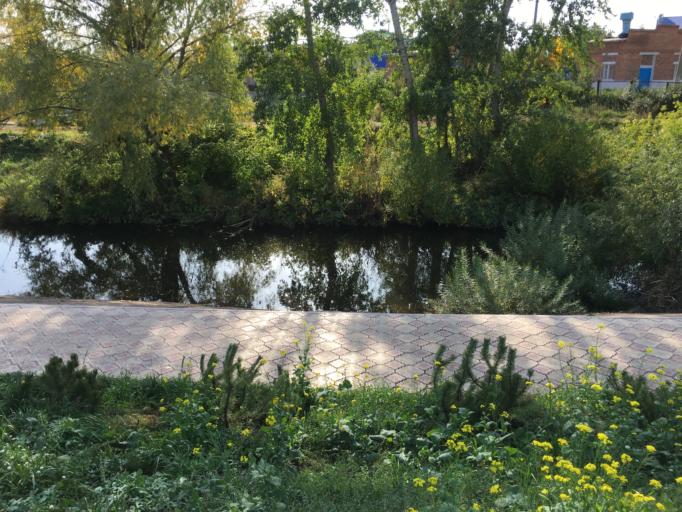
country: RU
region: Bashkortostan
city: Meleuz
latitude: 52.9595
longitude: 55.9353
